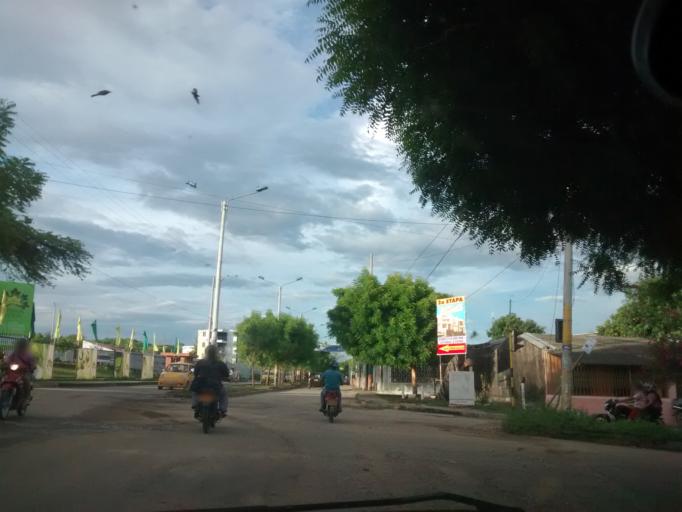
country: CO
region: Cundinamarca
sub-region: Girardot
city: Girardot City
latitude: 4.3149
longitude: -74.7934
